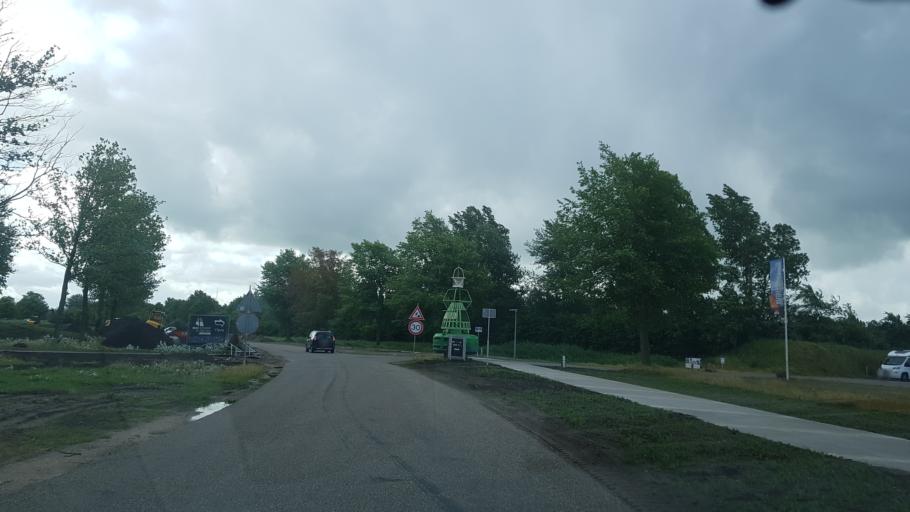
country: NL
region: Friesland
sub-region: Gemeente Dongeradeel
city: Anjum
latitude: 53.4044
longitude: 6.2125
